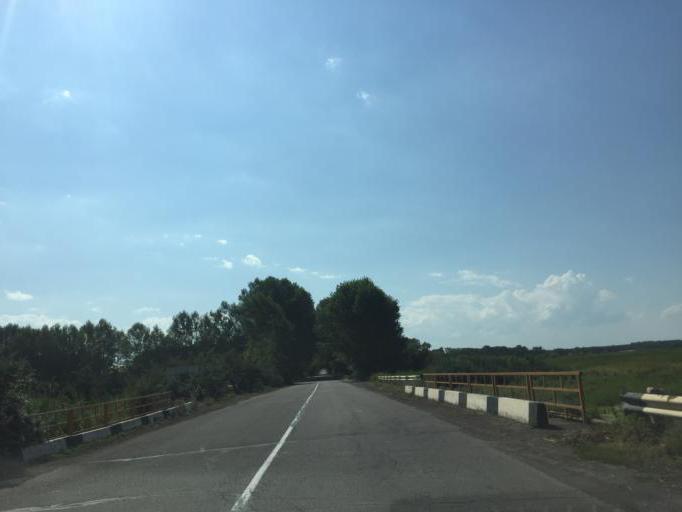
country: AM
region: Geghark'unik'i Marz
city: Artsvanist
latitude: 40.1601
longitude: 45.4952
